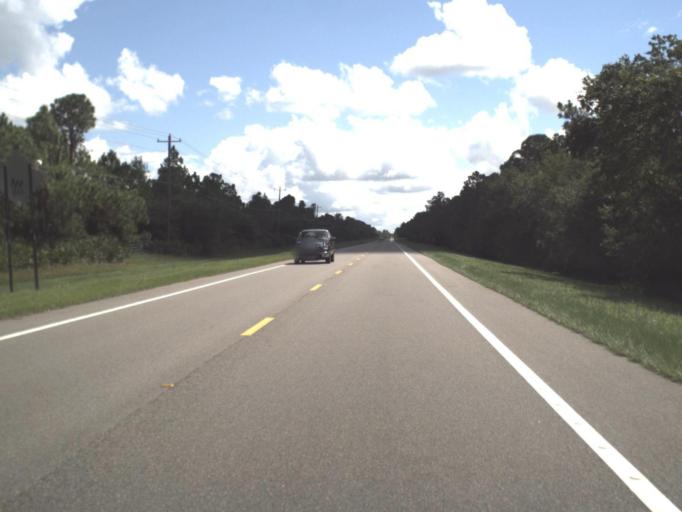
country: US
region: Florida
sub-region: Sarasota County
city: The Meadows
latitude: 27.4092
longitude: -82.3328
